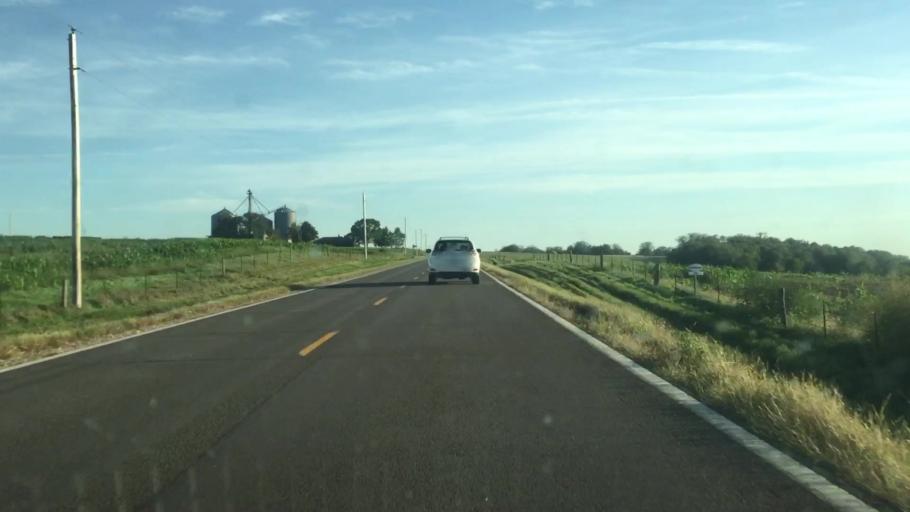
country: US
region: Kansas
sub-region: Brown County
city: Horton
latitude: 39.5787
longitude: -95.5270
